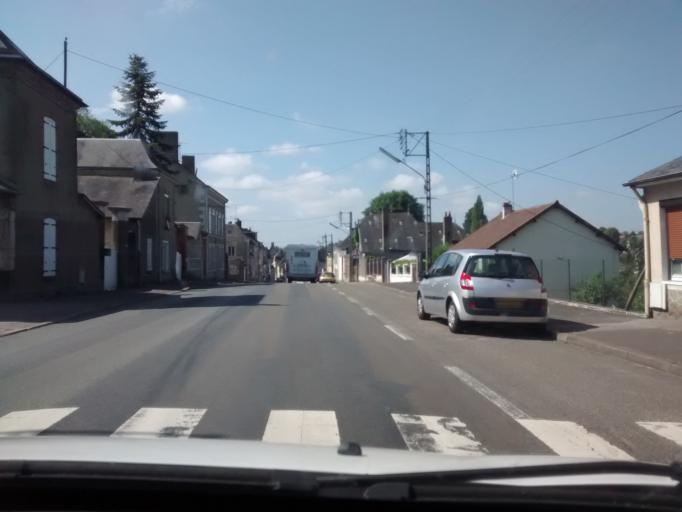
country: FR
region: Pays de la Loire
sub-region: Departement de la Sarthe
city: Saint-Calais
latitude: 47.9260
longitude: 0.7467
